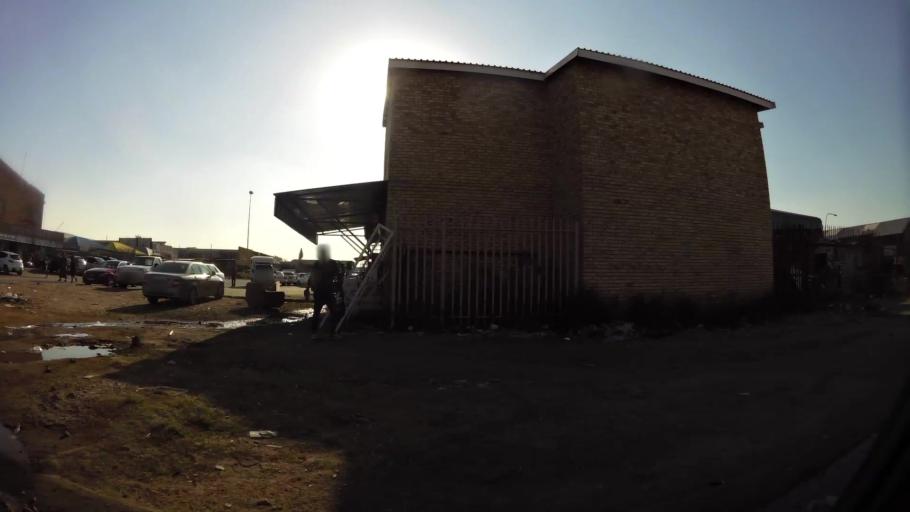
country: ZA
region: North-West
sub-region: Bojanala Platinum District Municipality
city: Rustenburg
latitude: -25.6501
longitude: 27.2414
